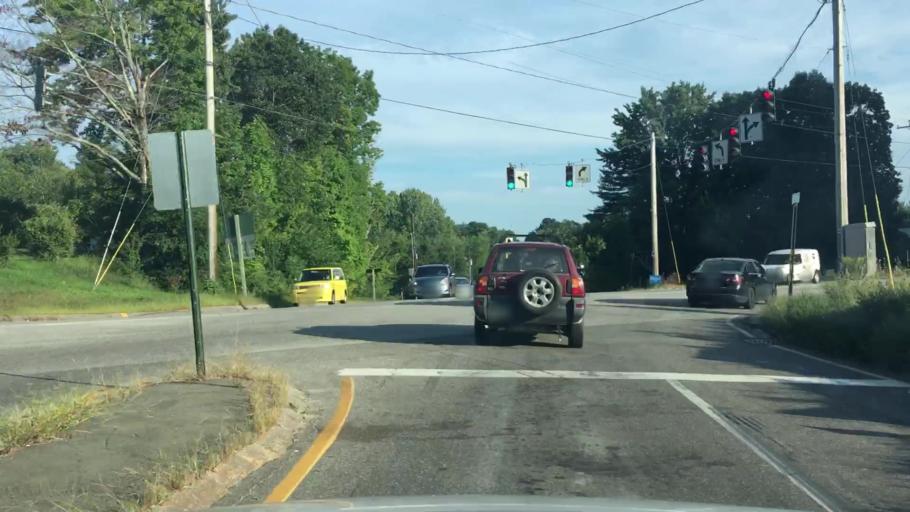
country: US
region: Maine
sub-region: Cumberland County
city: South Windham
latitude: 43.7454
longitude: -70.4254
